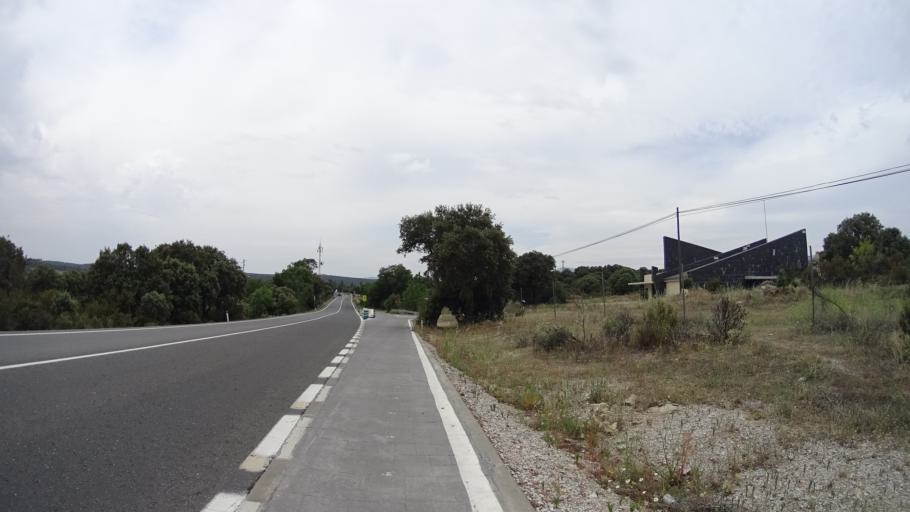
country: ES
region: Madrid
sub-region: Provincia de Madrid
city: Colmenarejo
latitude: 40.5425
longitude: -4.0422
